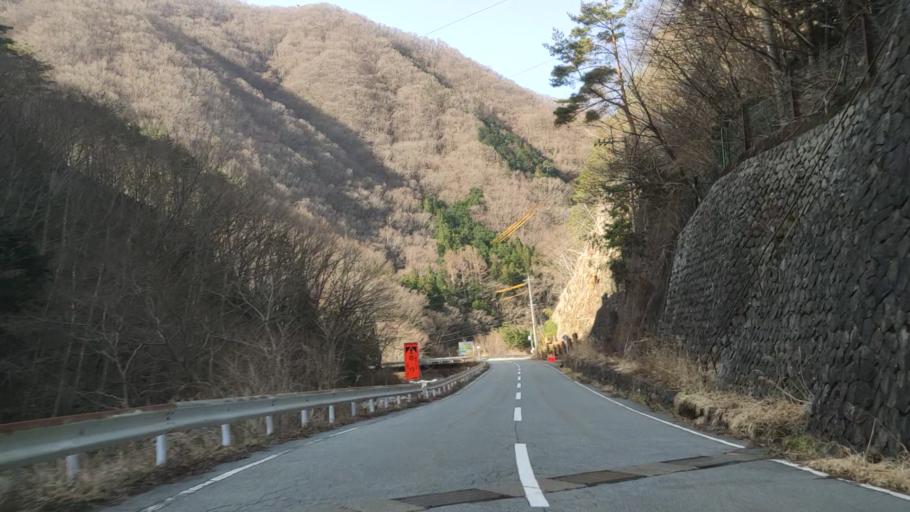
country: JP
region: Yamanashi
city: Fujikawaguchiko
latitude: 35.5413
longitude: 138.6406
